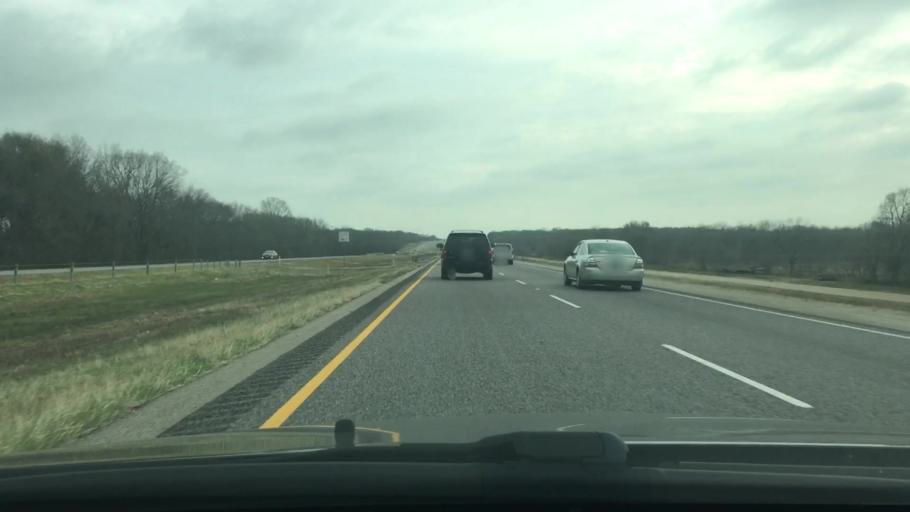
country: US
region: Texas
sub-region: Freestone County
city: Fairfield
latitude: 31.6532
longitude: -96.1606
